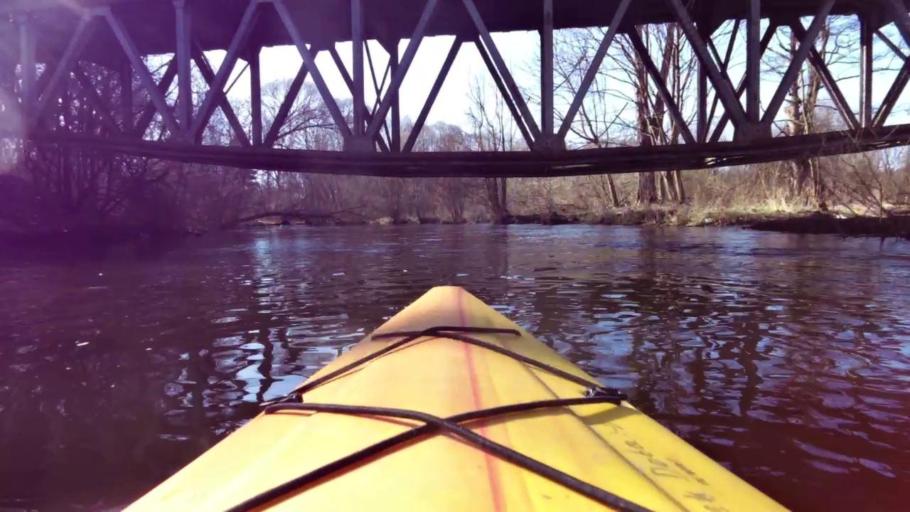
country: PL
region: West Pomeranian Voivodeship
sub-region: Powiat lobeski
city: Resko
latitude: 53.7663
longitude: 15.4085
